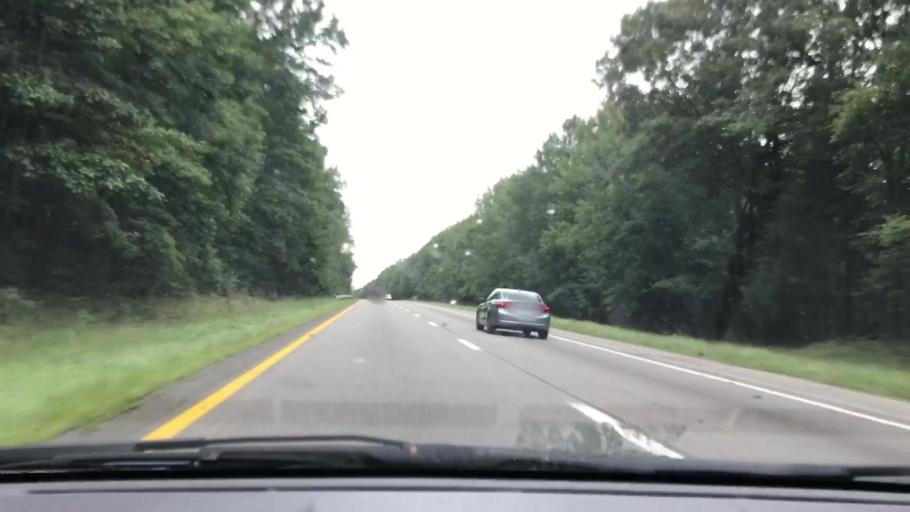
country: US
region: Virginia
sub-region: Louisa County
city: Louisa
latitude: 37.8595
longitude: -77.9988
